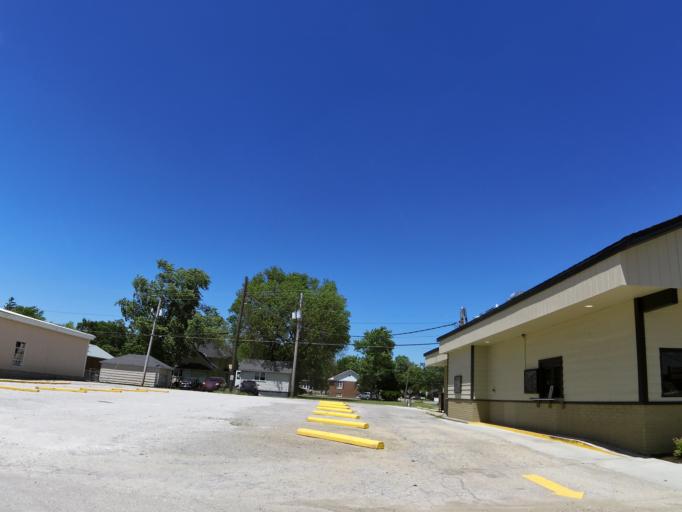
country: US
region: Illinois
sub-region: Livingston County
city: Forrest
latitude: 40.7495
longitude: -88.4109
